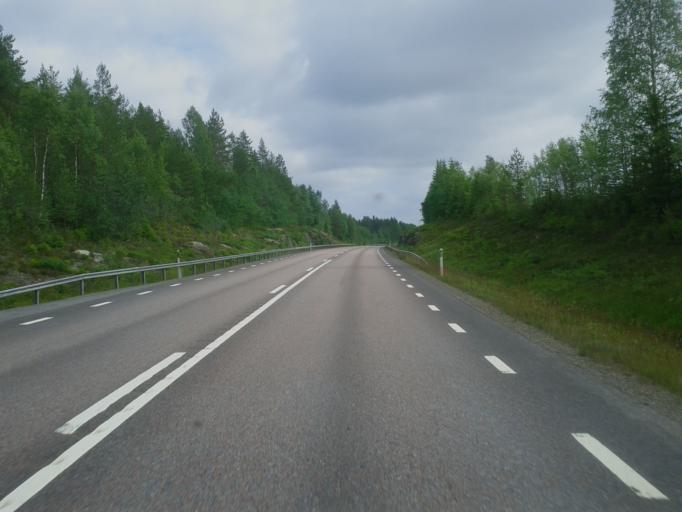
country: SE
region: Vaesterbotten
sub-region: Skelleftea Kommun
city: Burea
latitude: 64.3163
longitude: 21.1651
